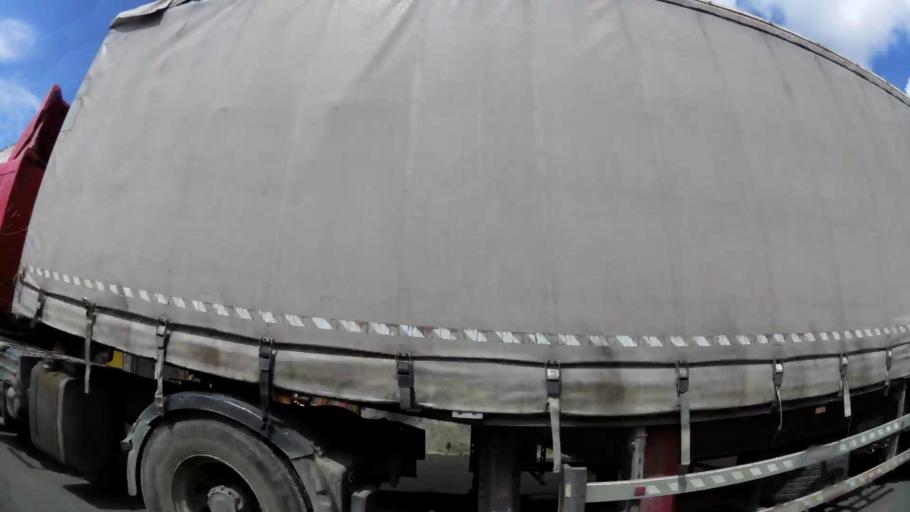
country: MA
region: Gharb-Chrarda-Beni Hssen
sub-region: Kenitra Province
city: Kenitra
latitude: 34.2648
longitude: -6.5707
